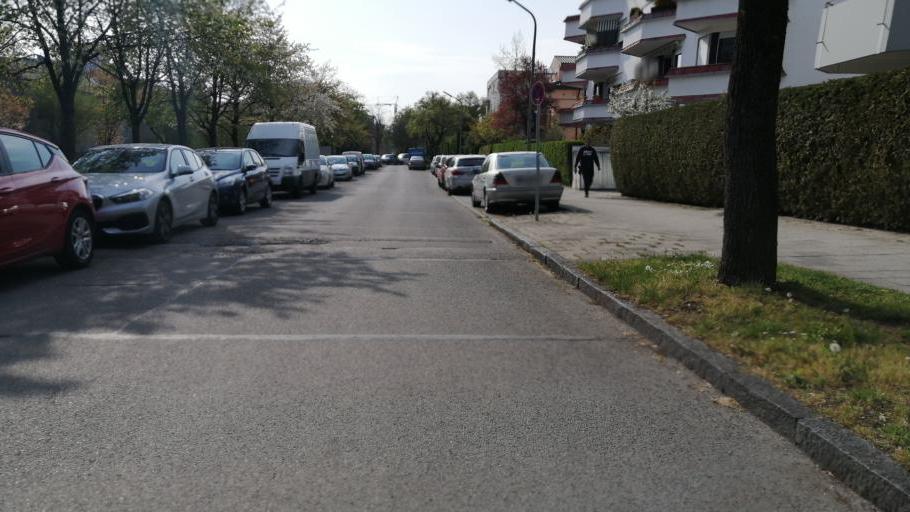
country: DE
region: Bavaria
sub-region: Upper Bavaria
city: Munich
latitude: 48.1806
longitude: 11.5772
